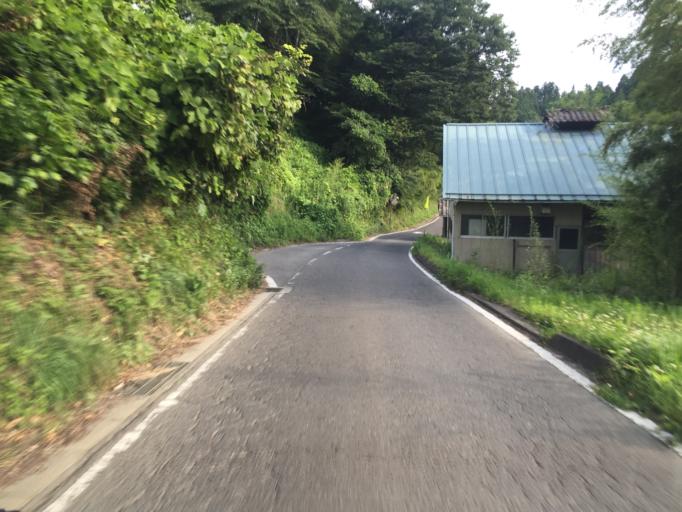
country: JP
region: Fukushima
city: Fukushima-shi
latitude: 37.6848
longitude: 140.5716
